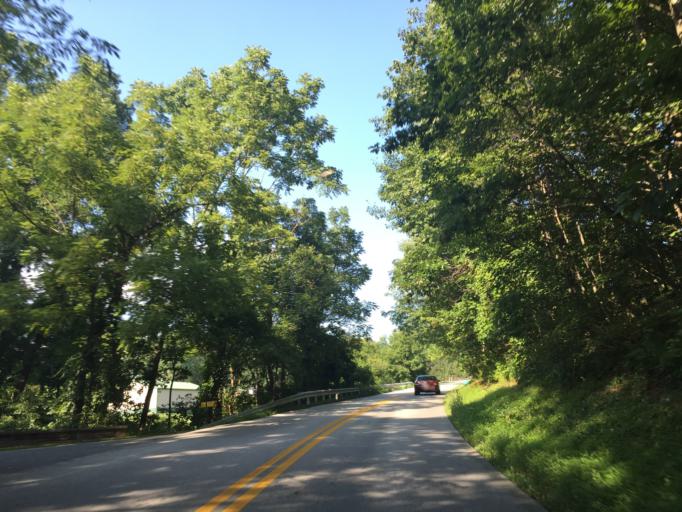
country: US
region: Maryland
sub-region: Carroll County
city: Manchester
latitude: 39.6310
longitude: -76.8887
